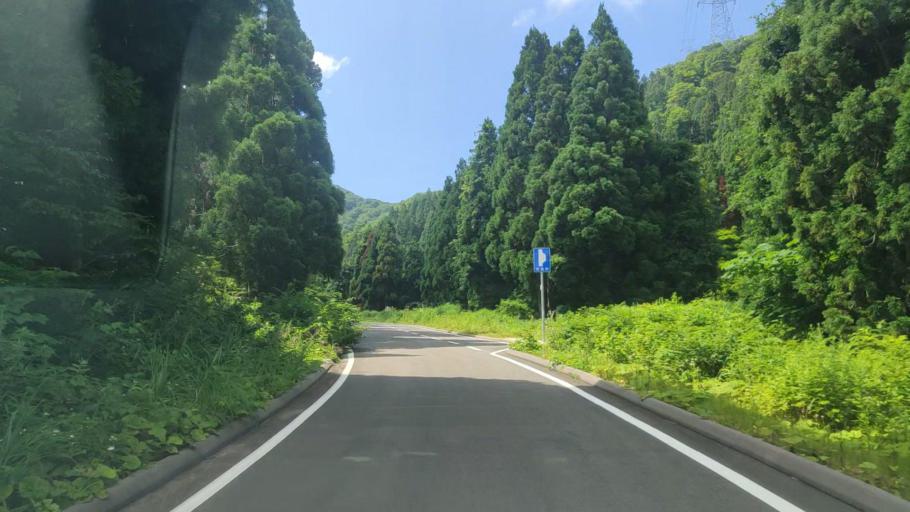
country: JP
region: Fukui
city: Katsuyama
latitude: 36.1574
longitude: 136.5264
